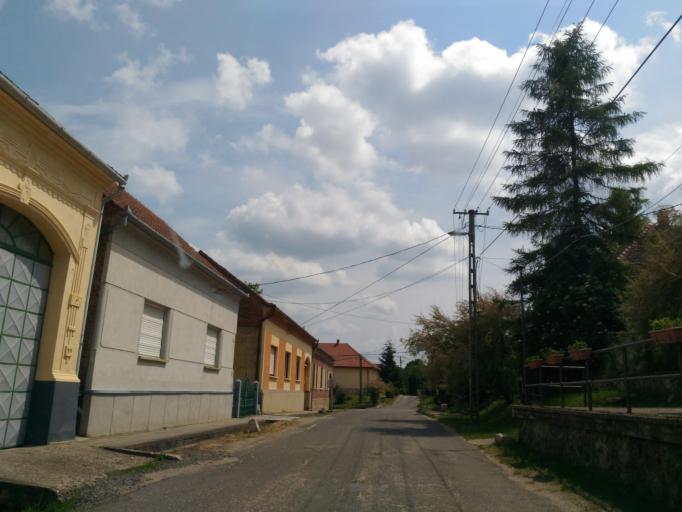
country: HU
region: Baranya
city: Komlo
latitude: 46.1953
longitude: 18.2278
